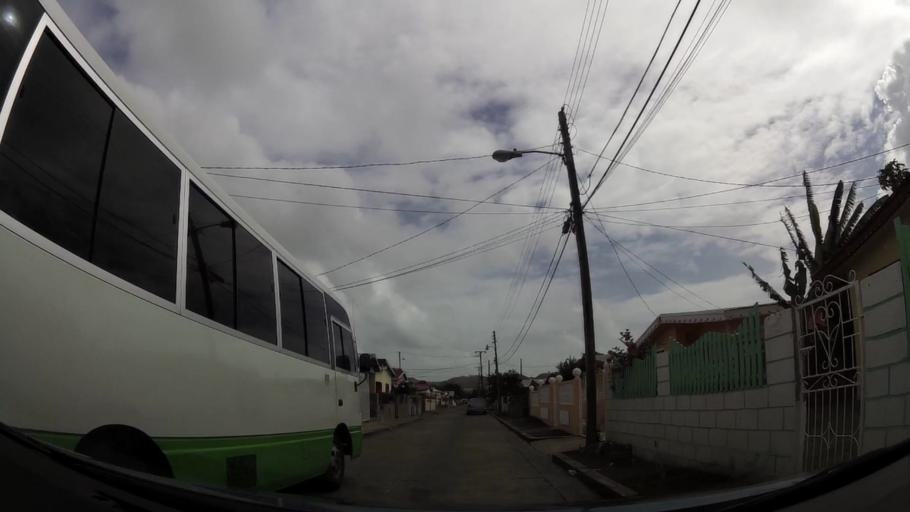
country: KN
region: Saint George Basseterre
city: Basseterre
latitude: 17.2988
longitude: -62.7177
